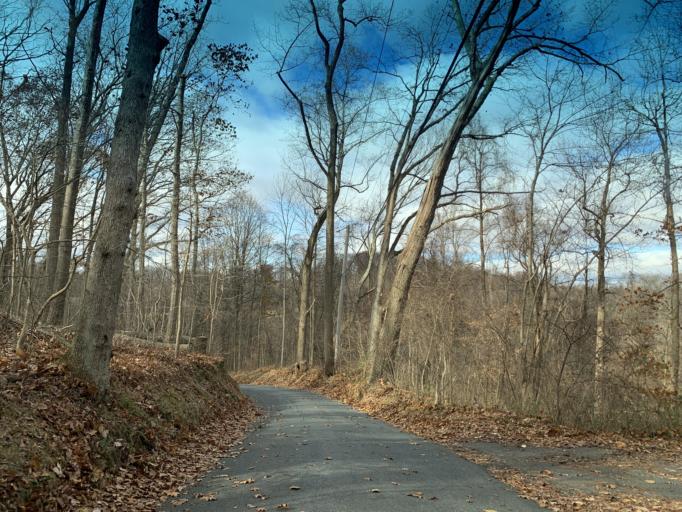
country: US
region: Maryland
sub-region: Harford County
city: Bel Air North
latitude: 39.5927
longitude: -76.4100
